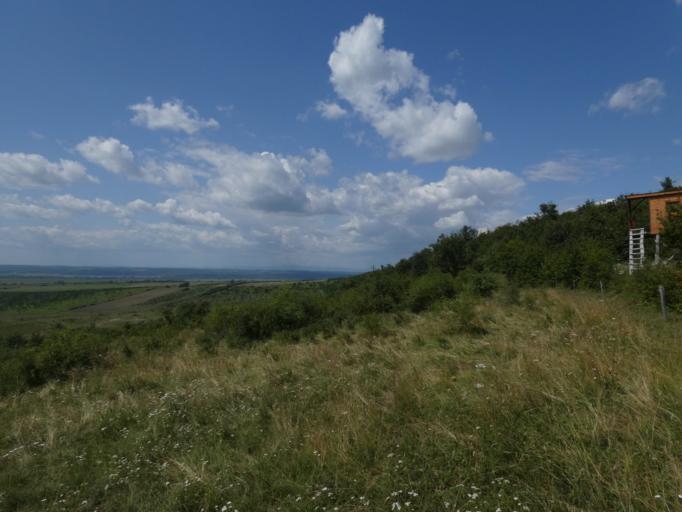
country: HU
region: Borsod-Abauj-Zemplen
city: Gonc
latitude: 48.3996
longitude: 21.2939
